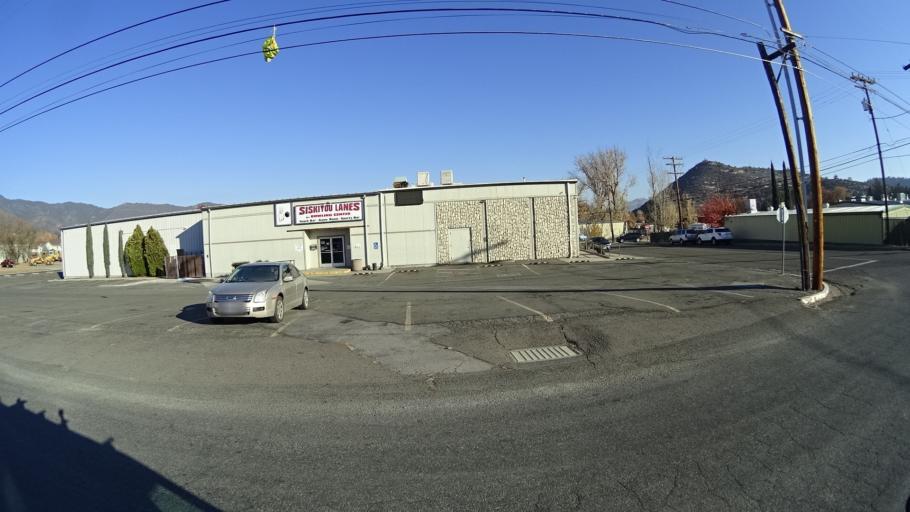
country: US
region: California
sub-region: Siskiyou County
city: Yreka
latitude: 41.7157
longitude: -122.6420
